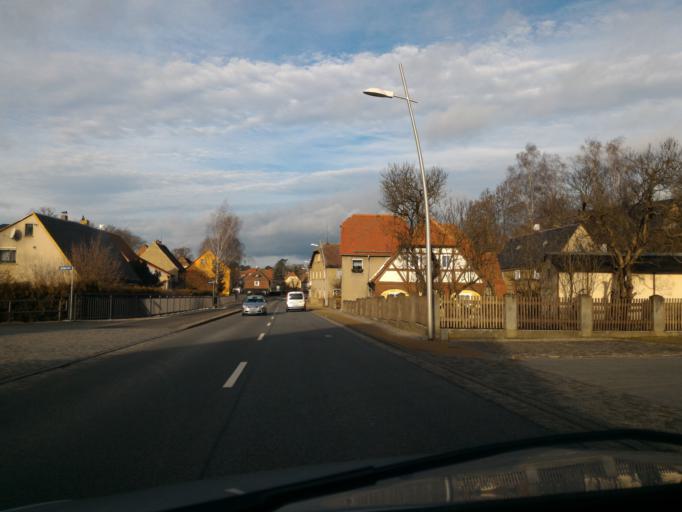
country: DE
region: Saxony
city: Ebersbach
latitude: 51.0066
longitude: 14.6006
